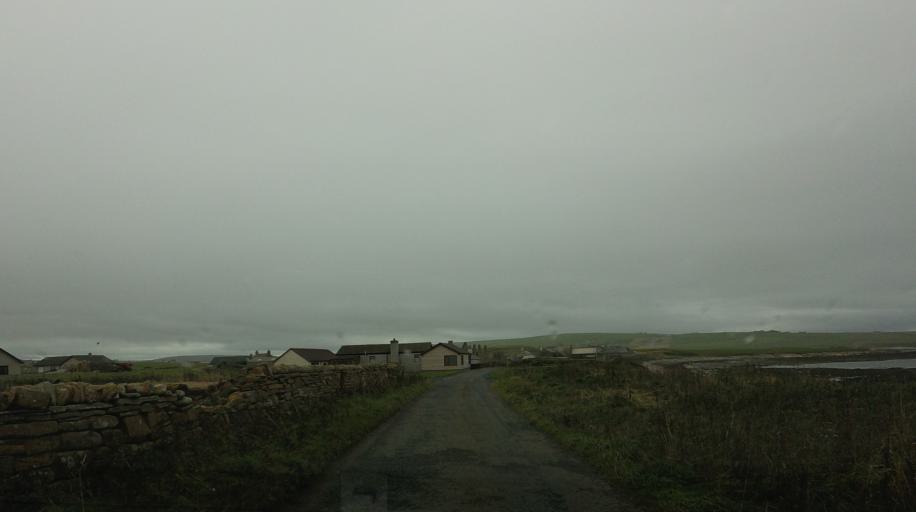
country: GB
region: Scotland
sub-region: Orkney Islands
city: Stromness
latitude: 59.1324
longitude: -3.3174
